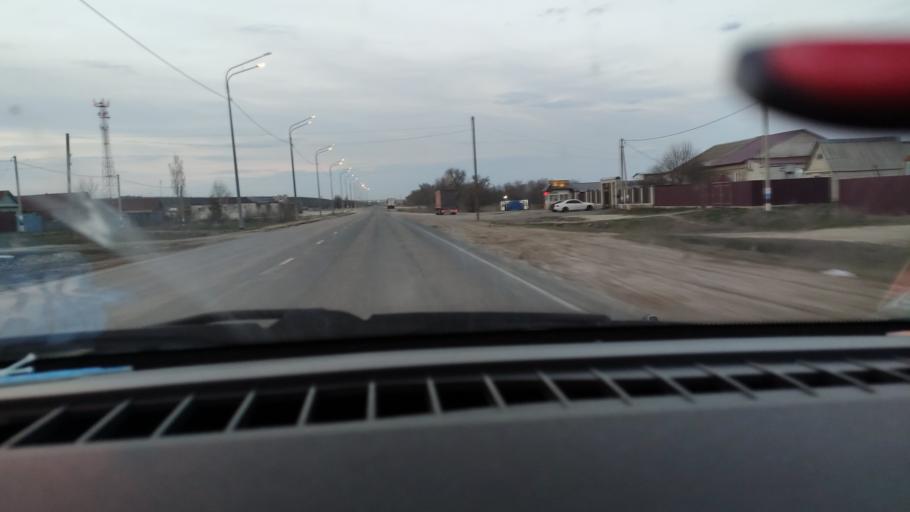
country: RU
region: Saratov
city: Sinodskoye
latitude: 51.9984
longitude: 46.6759
